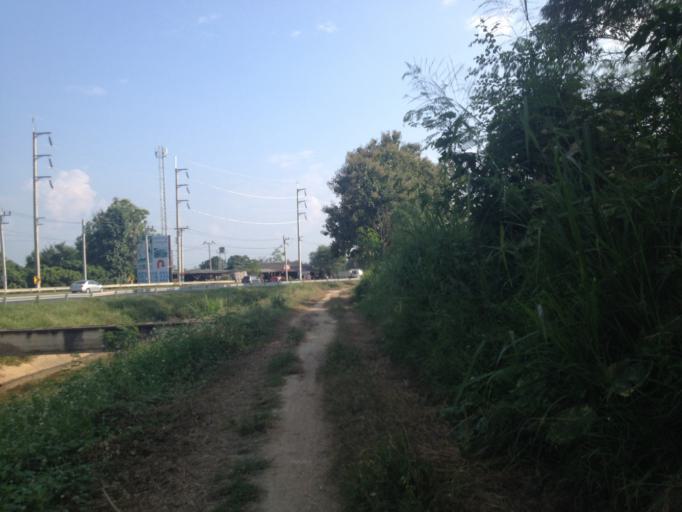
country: TH
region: Chiang Mai
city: Hang Dong
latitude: 18.7204
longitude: 98.9281
